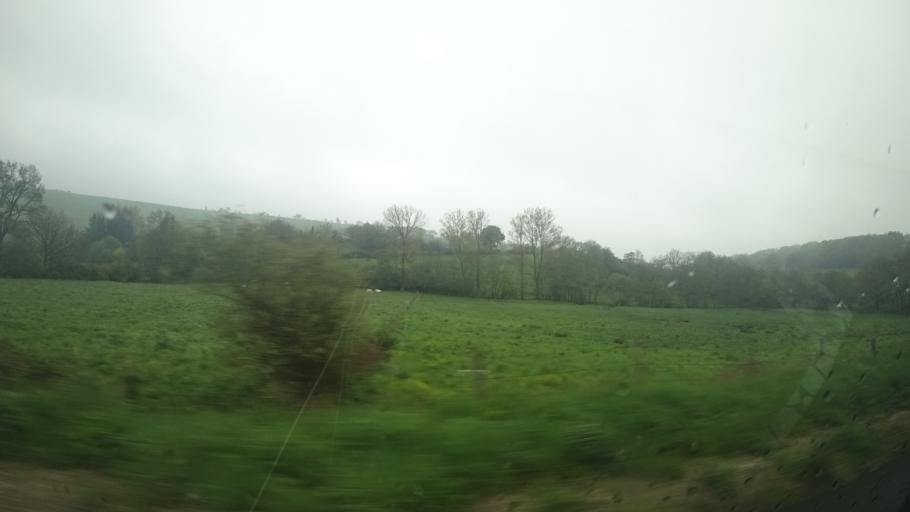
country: FR
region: Midi-Pyrenees
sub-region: Departement de l'Aveyron
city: Laissac
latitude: 44.2686
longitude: 2.9059
